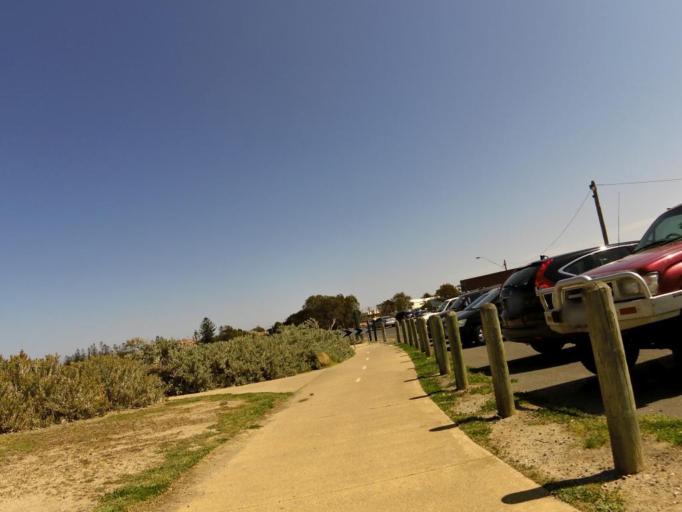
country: AU
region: Victoria
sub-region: Hobsons Bay
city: Seaholme
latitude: -37.8680
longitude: 144.8456
